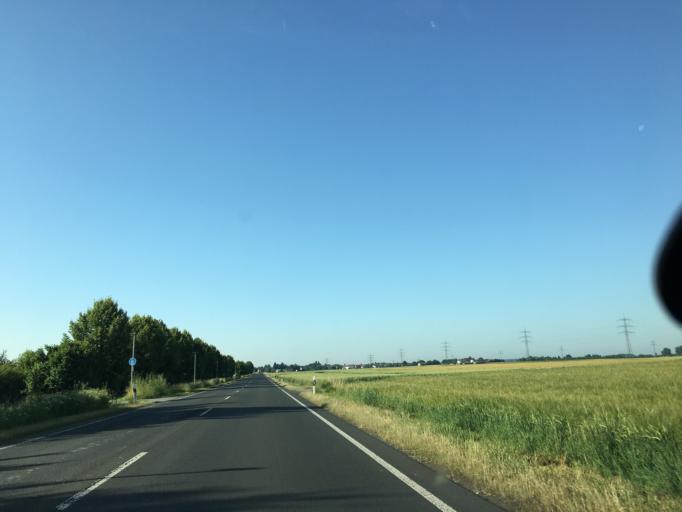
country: DE
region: Hesse
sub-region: Regierungsbezirk Darmstadt
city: Gross-Gerau
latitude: 49.8927
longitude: 8.4801
